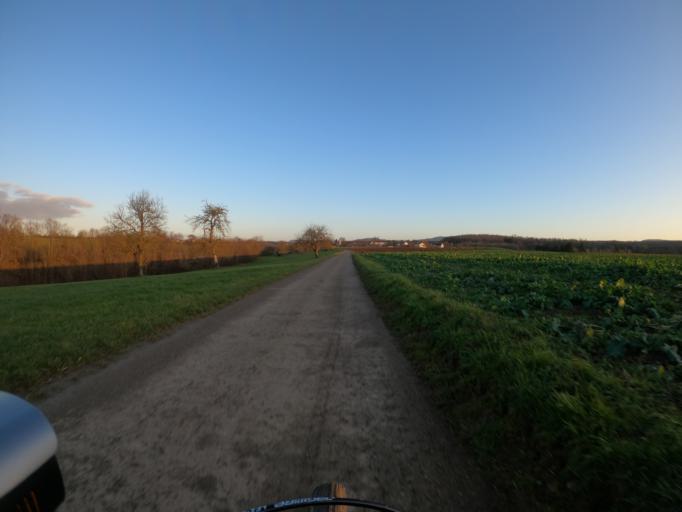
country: DE
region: Baden-Wuerttemberg
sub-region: Regierungsbezirk Stuttgart
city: Schlierbach
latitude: 48.6745
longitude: 9.5044
